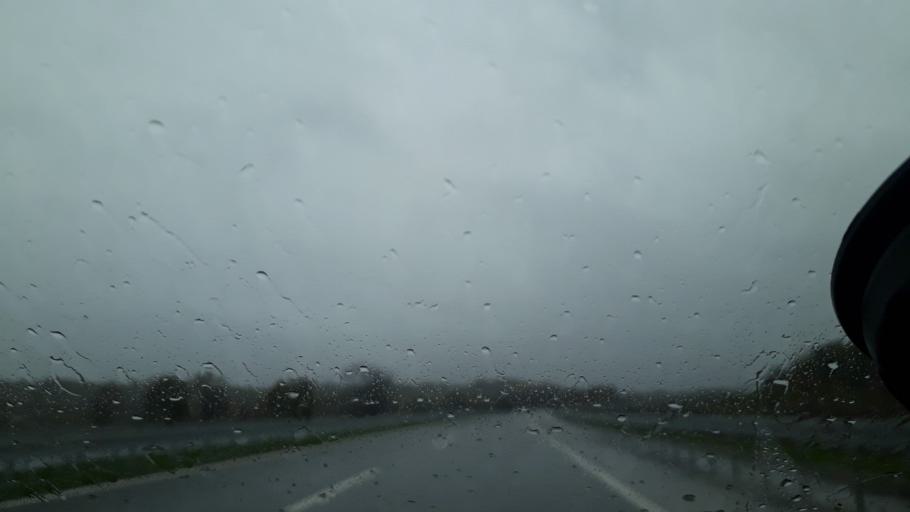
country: BA
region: Republika Srpska
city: Stanari
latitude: 44.8190
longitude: 17.8176
